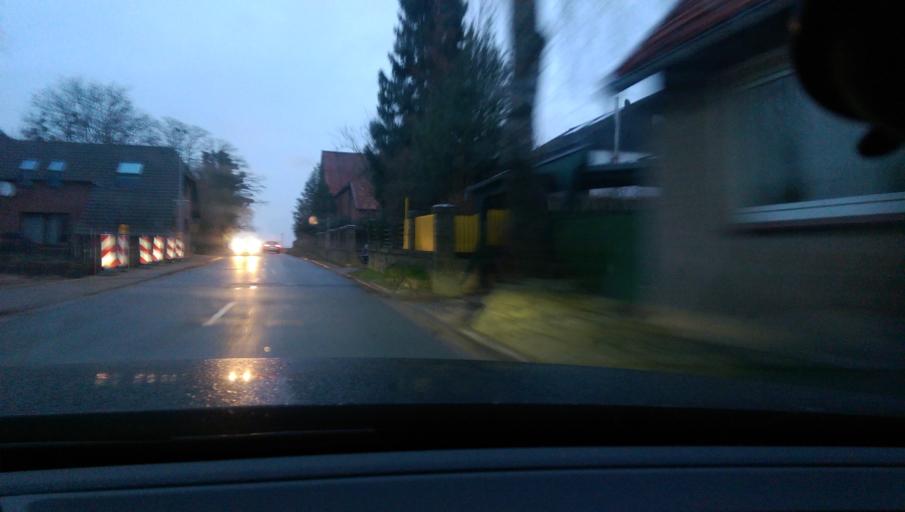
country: DE
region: Lower Saxony
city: Wennigsen
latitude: 52.2999
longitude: 9.5672
